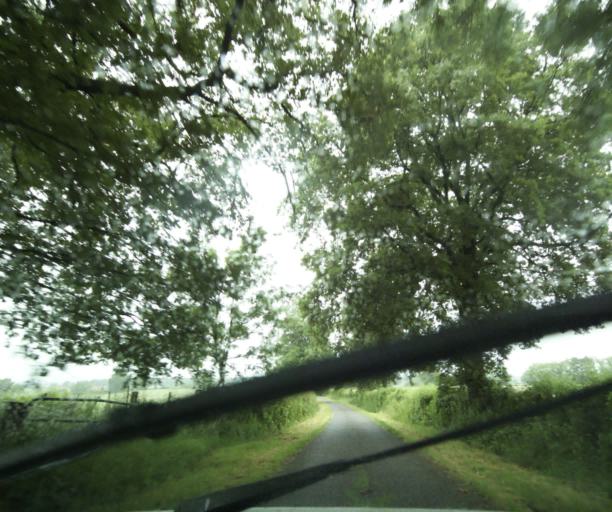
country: FR
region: Bourgogne
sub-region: Departement de Saone-et-Loire
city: Paray-le-Monial
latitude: 46.4661
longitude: 4.1997
